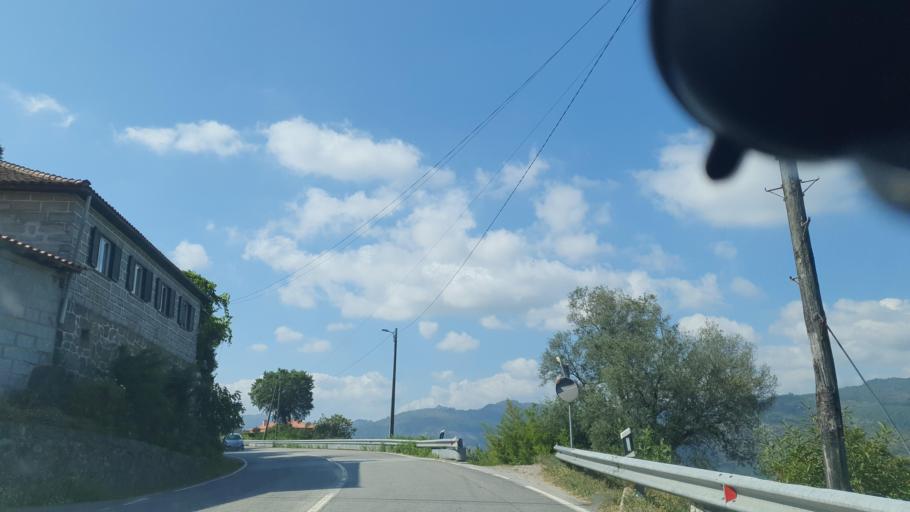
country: PT
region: Braga
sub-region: Vieira do Minho
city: Vieira do Minho
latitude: 41.6731
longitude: -8.1450
